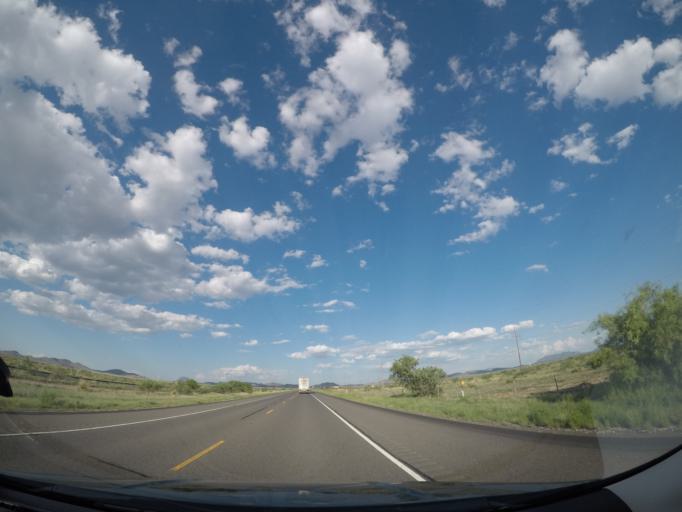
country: US
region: Texas
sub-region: Presidio County
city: Marfa
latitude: 30.2762
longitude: -103.8897
